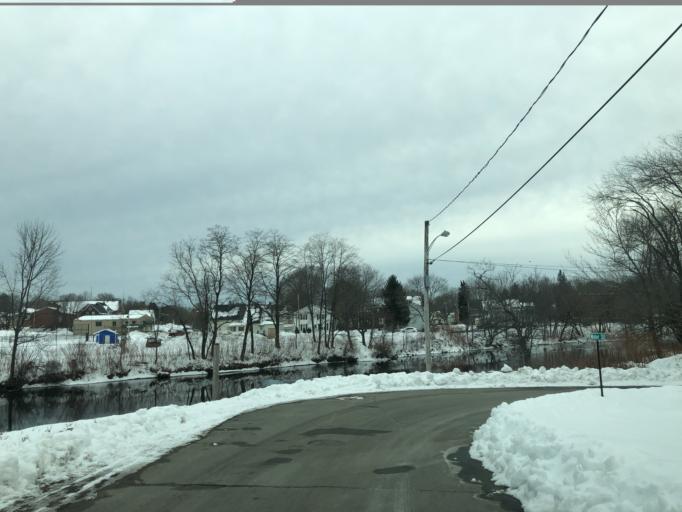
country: US
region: Maine
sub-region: Cumberland County
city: Westbrook
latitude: 43.6813
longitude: -70.3569
